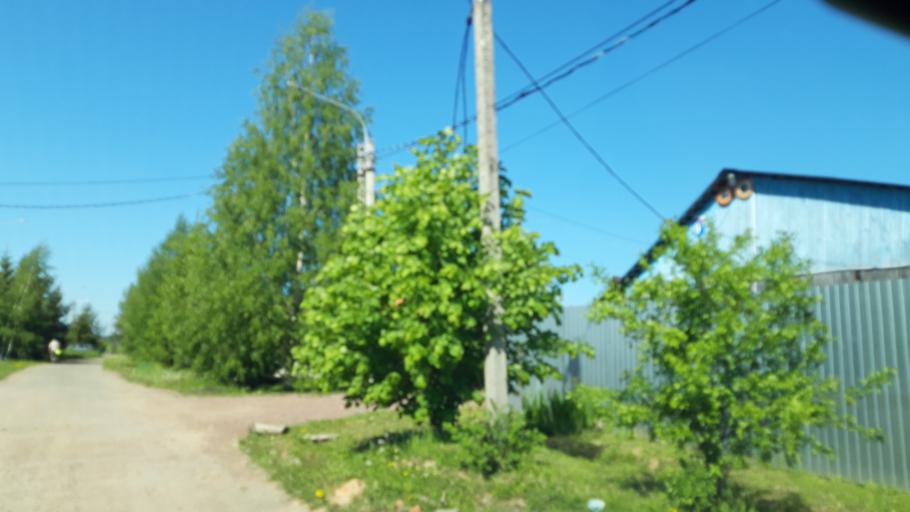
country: RU
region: Moskovskaya
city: Lozhki
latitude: 56.0666
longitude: 37.1181
